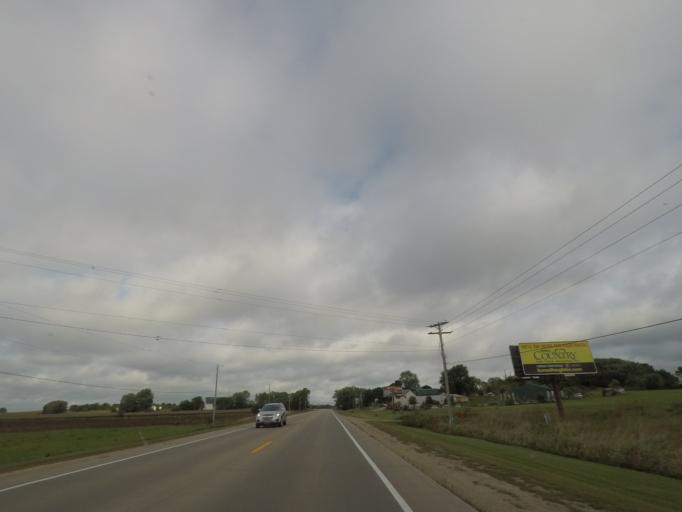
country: US
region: Wisconsin
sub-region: Jefferson County
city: Cambridge
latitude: 43.0158
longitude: -89.0331
